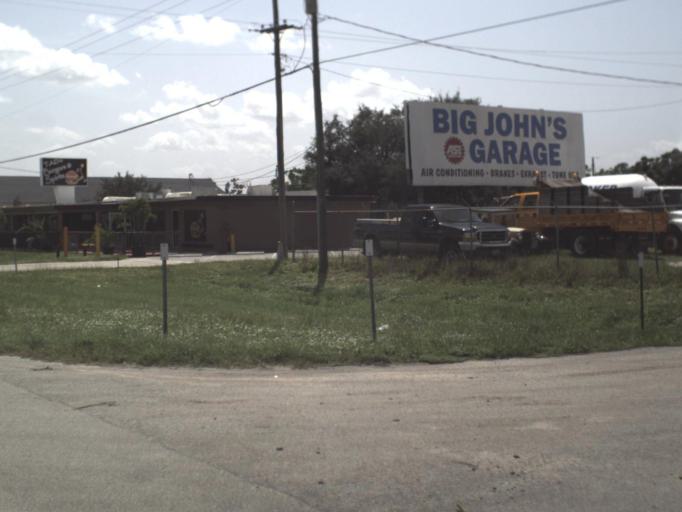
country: US
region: Florida
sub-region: Highlands County
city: Sebring
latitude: 27.4636
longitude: -81.4334
